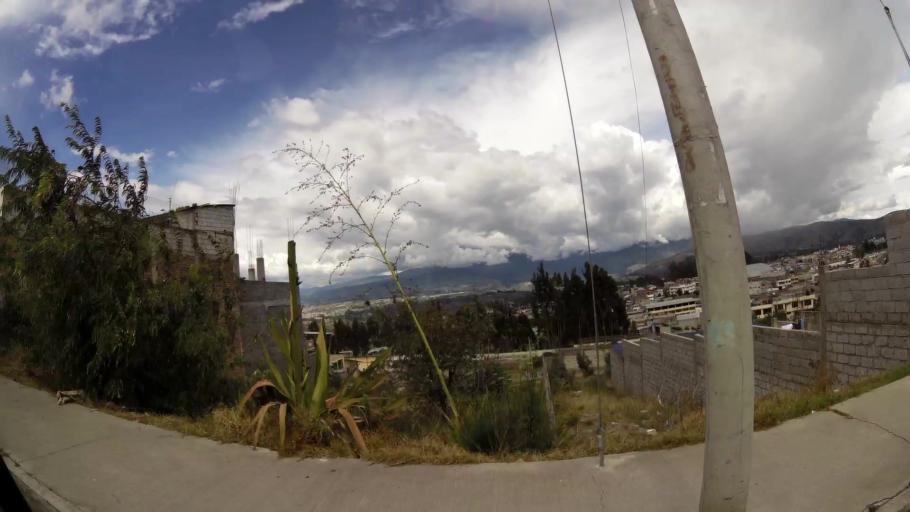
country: EC
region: Tungurahua
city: Ambato
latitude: -1.2606
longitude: -78.6179
